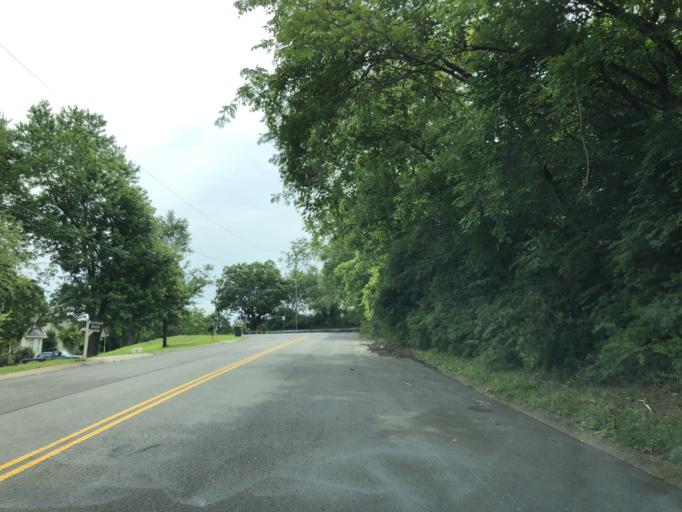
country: US
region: Tennessee
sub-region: Davidson County
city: Goodlettsville
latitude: 36.2825
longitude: -86.7106
